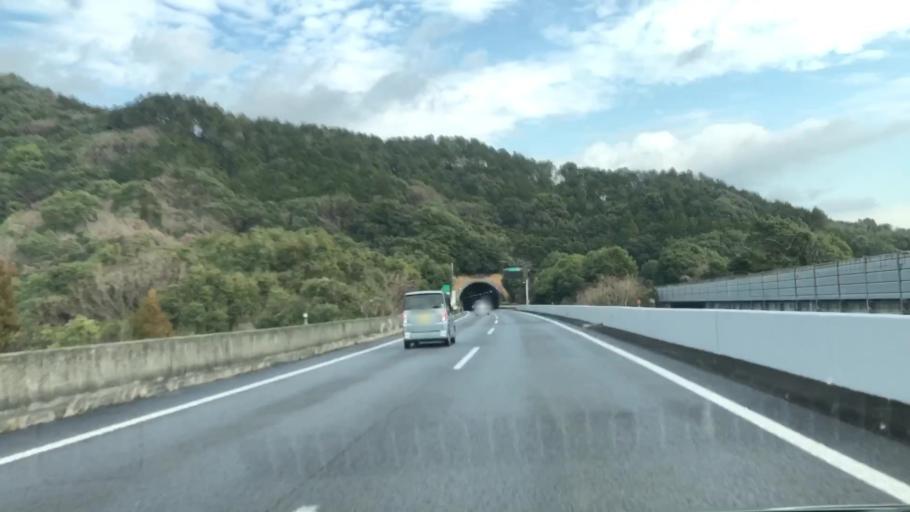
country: JP
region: Saga Prefecture
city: Kanzakimachi-kanzaki
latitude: 33.3396
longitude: 130.3524
